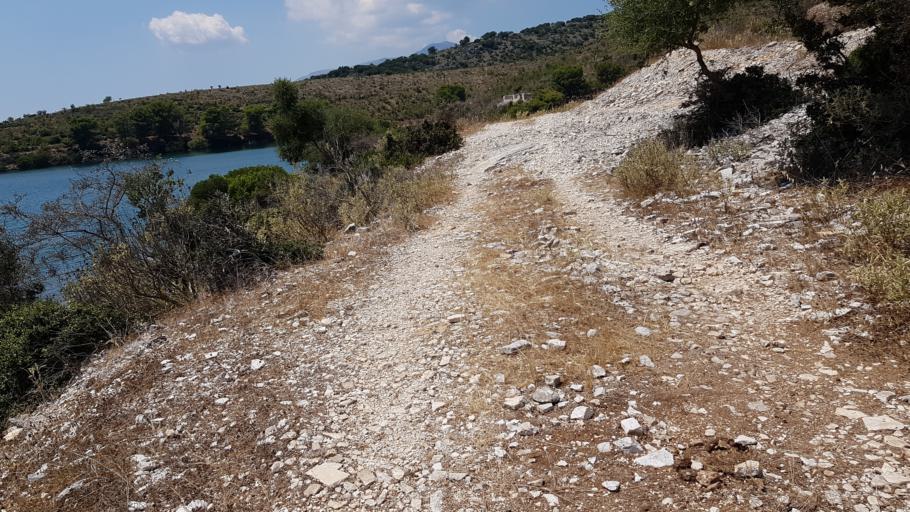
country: AL
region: Vlore
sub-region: Rrethi i Sarandes
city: Xarre
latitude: 39.7493
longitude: 19.9936
